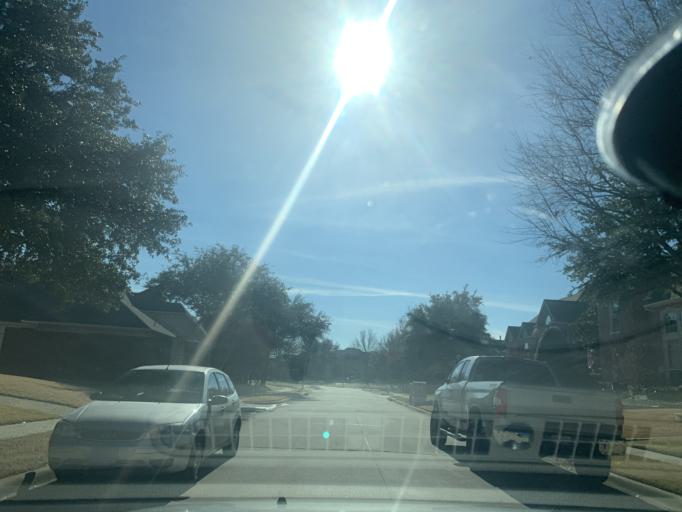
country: US
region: Texas
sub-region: Denton County
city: The Colony
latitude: 33.0539
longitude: -96.8236
